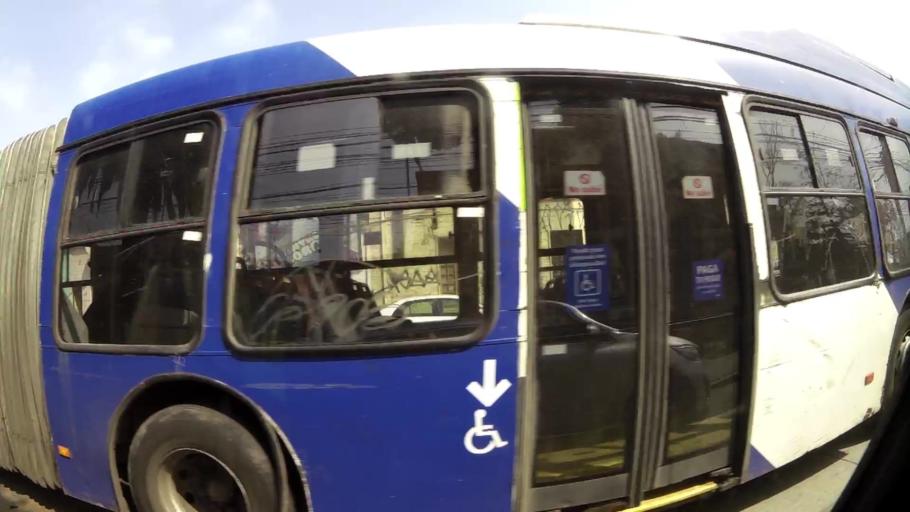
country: CL
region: Santiago Metropolitan
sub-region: Provincia de Santiago
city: Santiago
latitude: -33.4633
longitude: -70.6427
